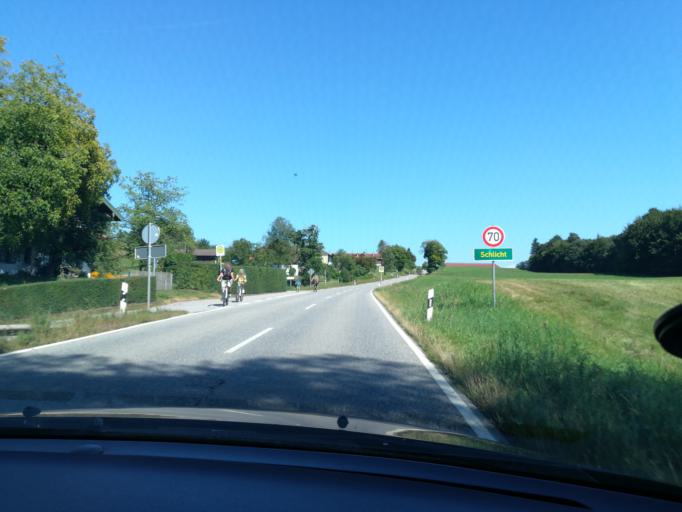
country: DE
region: Bavaria
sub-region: Upper Bavaria
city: Rimsting
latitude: 47.9105
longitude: 12.3498
